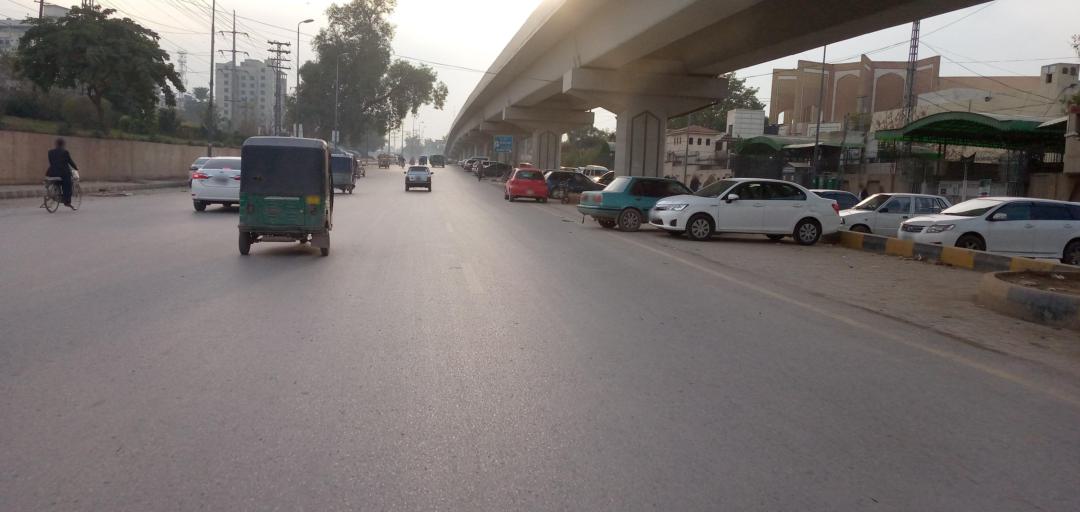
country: PK
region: Khyber Pakhtunkhwa
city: Peshawar
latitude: 34.0128
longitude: 71.5659
